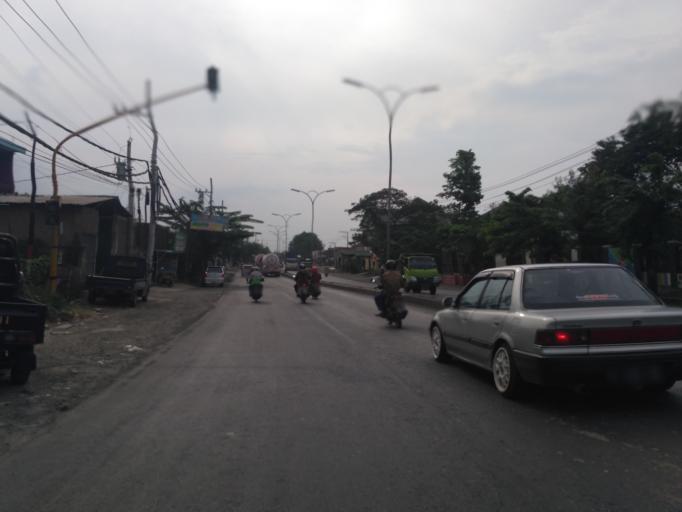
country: ID
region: Central Java
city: Semarang
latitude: -6.9788
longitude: 110.3326
